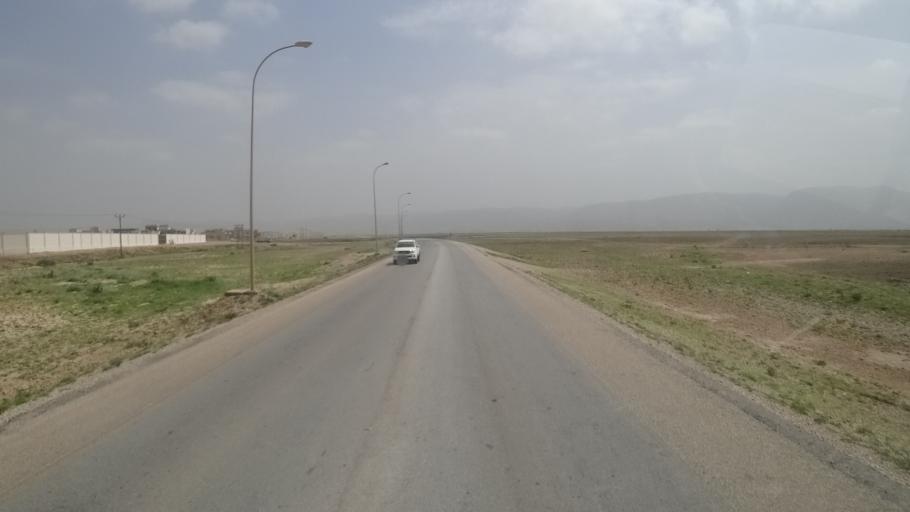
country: OM
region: Zufar
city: Salalah
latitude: 17.0658
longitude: 54.2168
